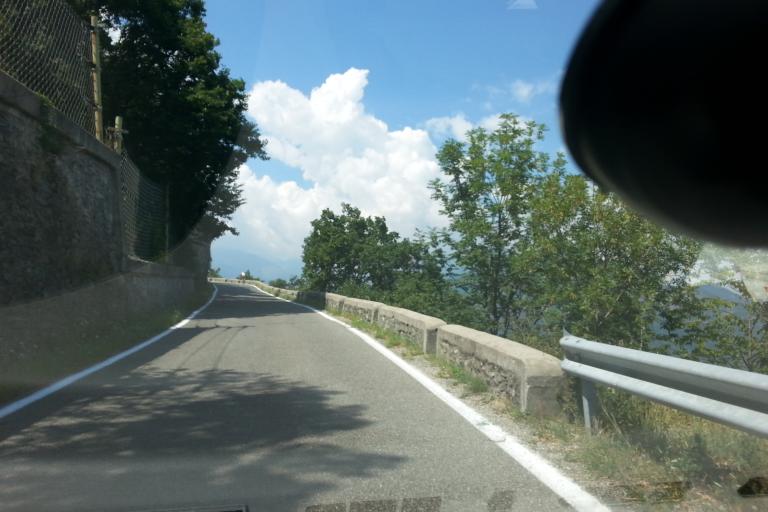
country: IT
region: Piedmont
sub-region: Provincia di Torino
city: Sant'Ambrogio di Torino
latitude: 45.0932
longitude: 7.3538
